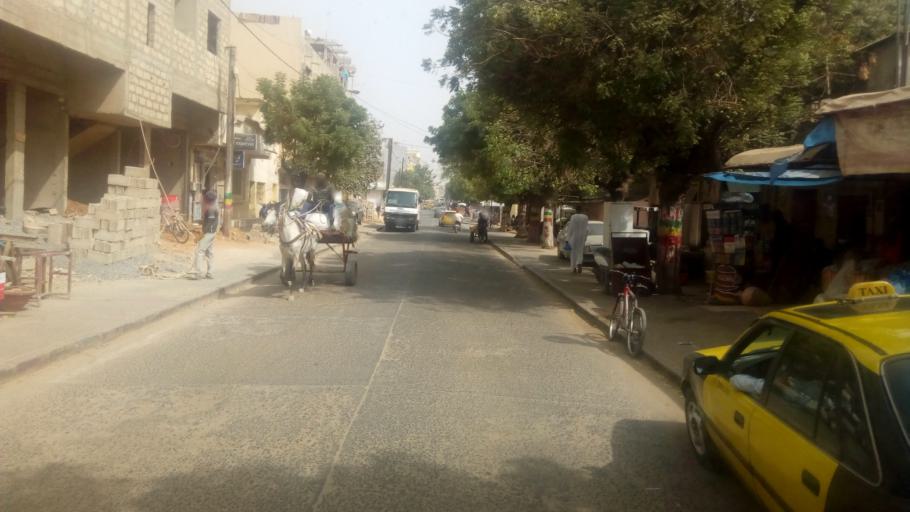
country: SN
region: Dakar
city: Grand Dakar
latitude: 14.7247
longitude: -17.4529
